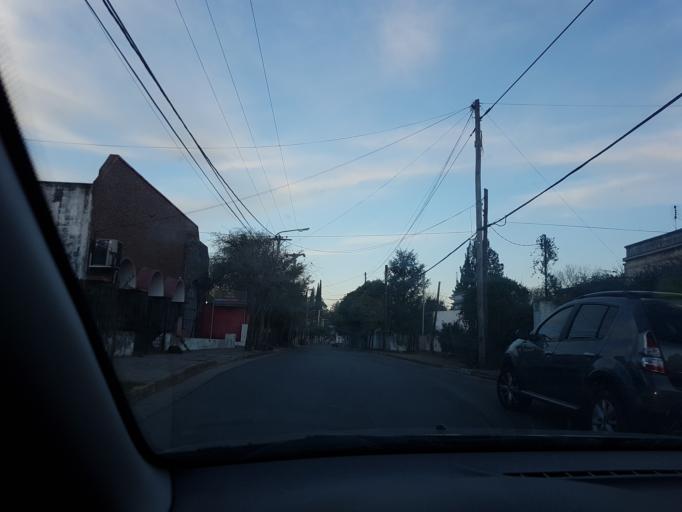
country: AR
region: Cordoba
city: Villa Allende
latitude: -31.2889
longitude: -64.2957
